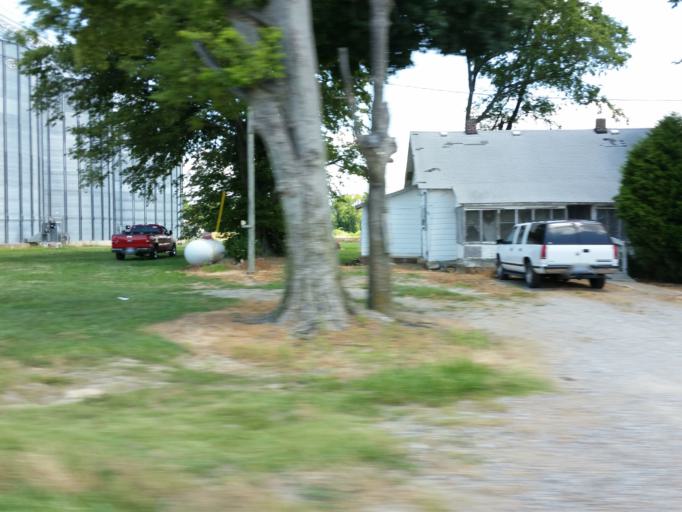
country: US
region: Kentucky
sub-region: Fulton County
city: Hickman
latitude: 36.5552
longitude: -89.2793
